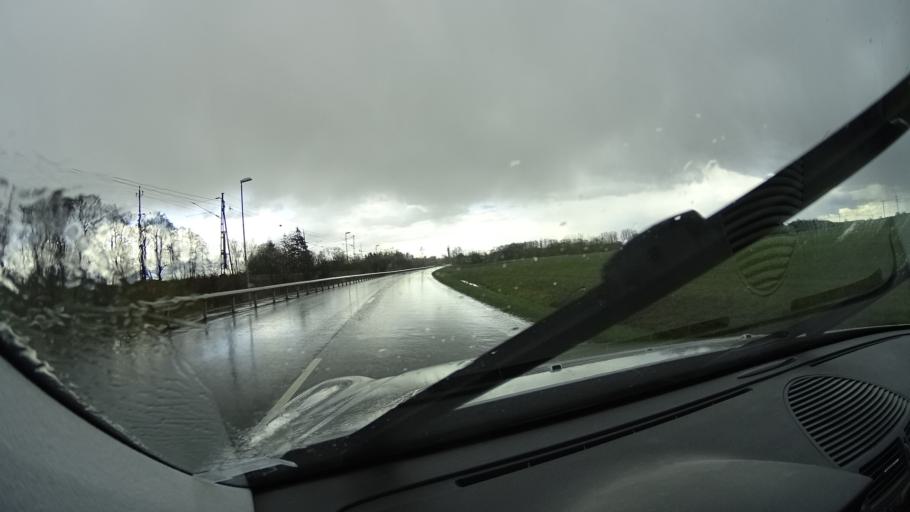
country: SE
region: Skane
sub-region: Lunds Kommun
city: Lund
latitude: 55.7761
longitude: 13.2341
